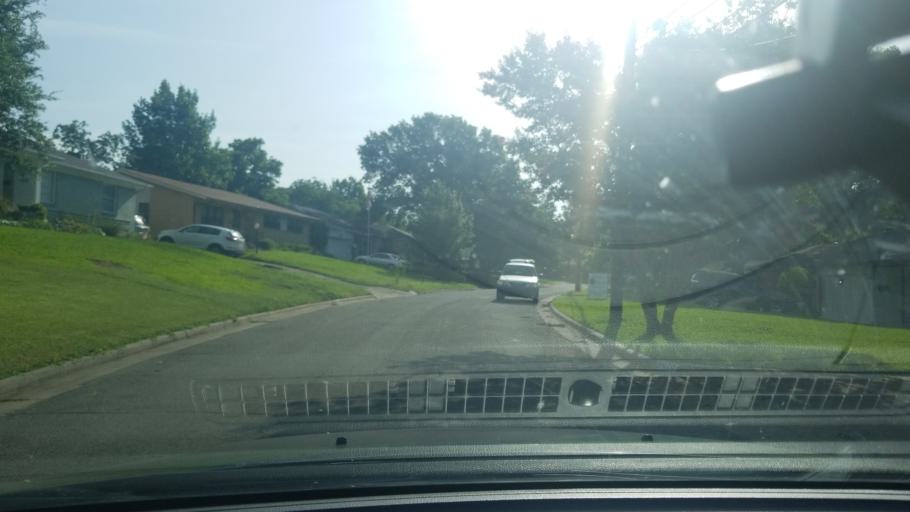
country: US
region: Texas
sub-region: Dallas County
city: Highland Park
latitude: 32.8003
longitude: -96.7048
